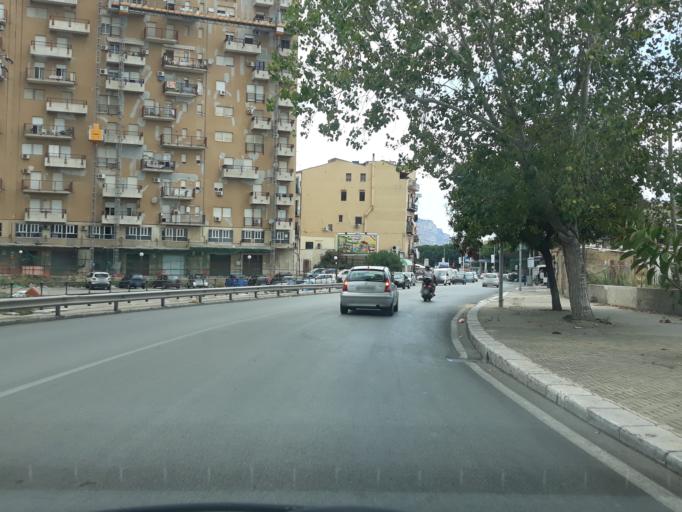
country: IT
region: Sicily
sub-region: Palermo
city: Ciaculli
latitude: 38.1107
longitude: 13.3786
